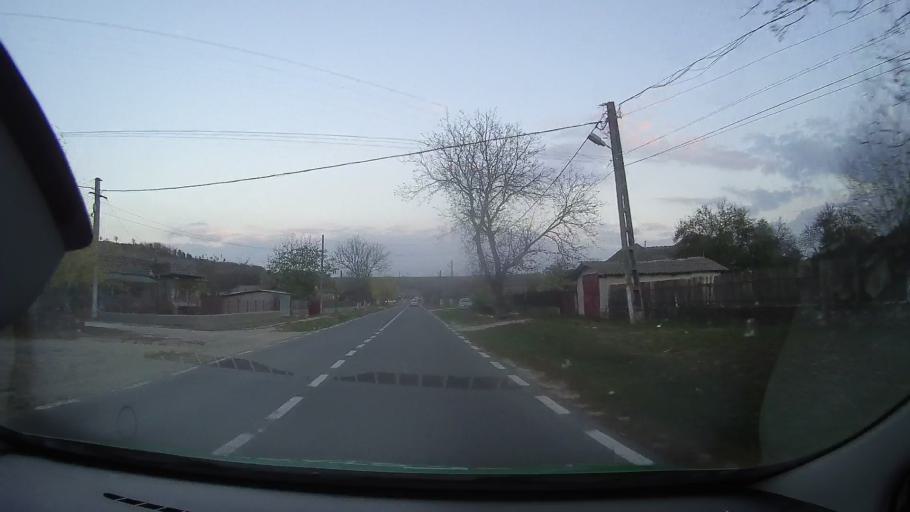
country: RO
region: Constanta
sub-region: Comuna Baneasa
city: Baneasa
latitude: 44.0751
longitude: 27.6851
